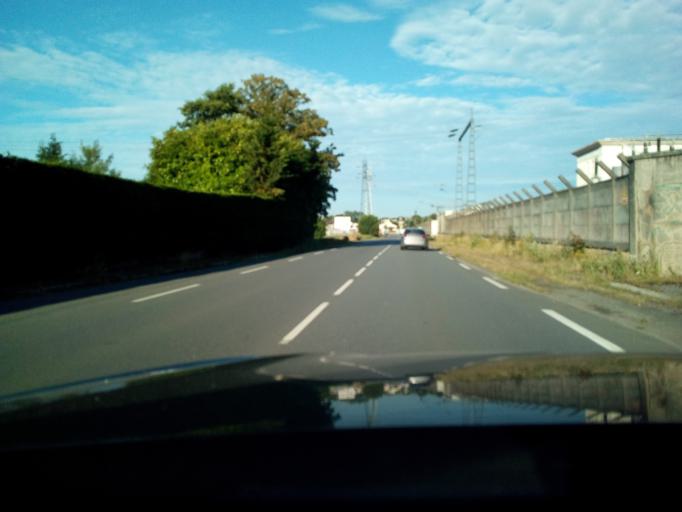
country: FR
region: Brittany
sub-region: Departement du Finistere
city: Landerneau
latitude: 48.4606
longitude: -4.2352
